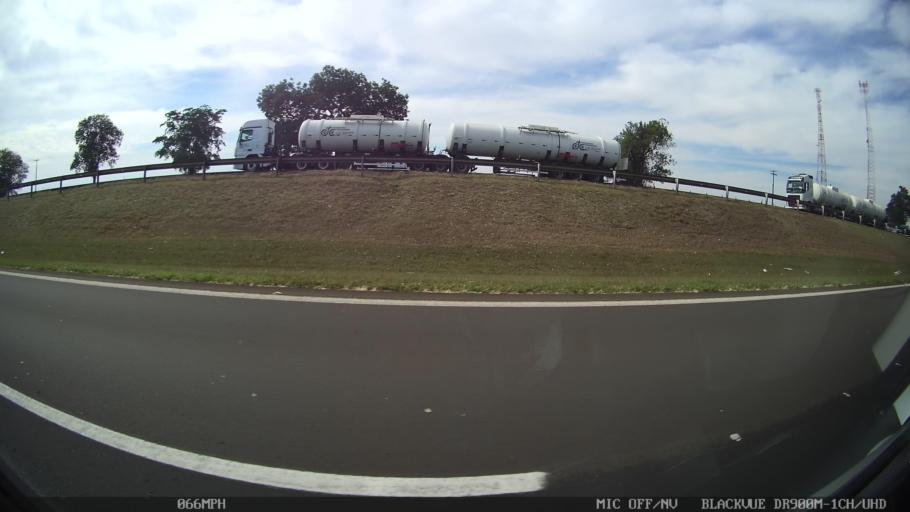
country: BR
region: Sao Paulo
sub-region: Matao
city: Matao
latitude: -21.5970
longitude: -48.4367
